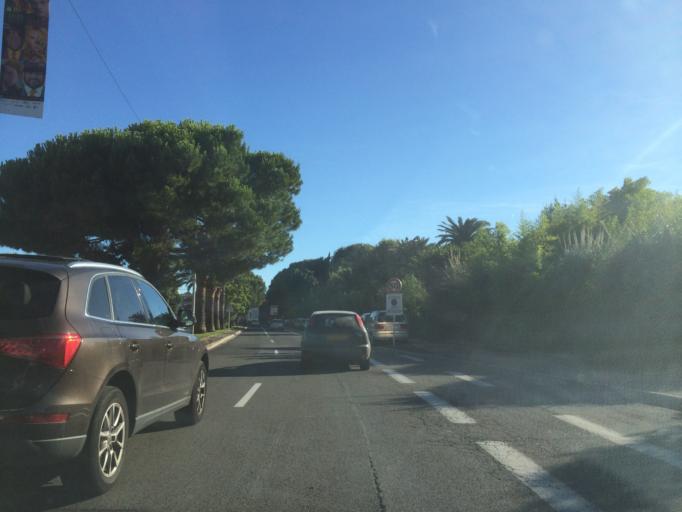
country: FR
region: Provence-Alpes-Cote d'Azur
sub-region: Departement des Alpes-Maritimes
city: Antibes
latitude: 43.5889
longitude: 7.1223
